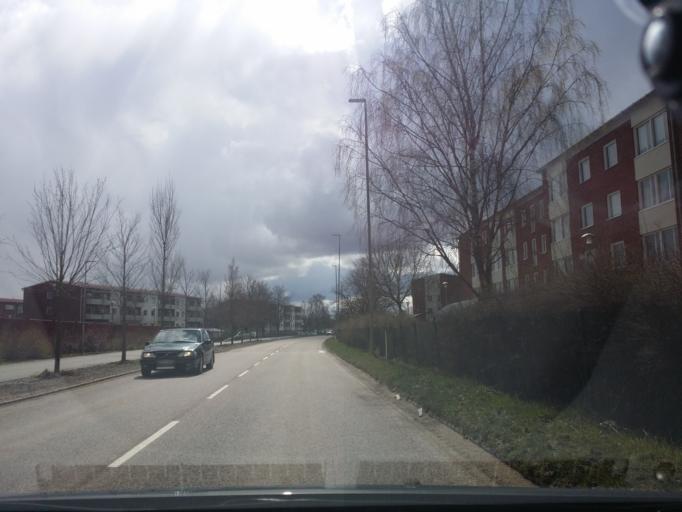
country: SE
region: Vaestmanland
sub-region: Sala Kommun
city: Sala
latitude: 59.9252
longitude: 16.5898
